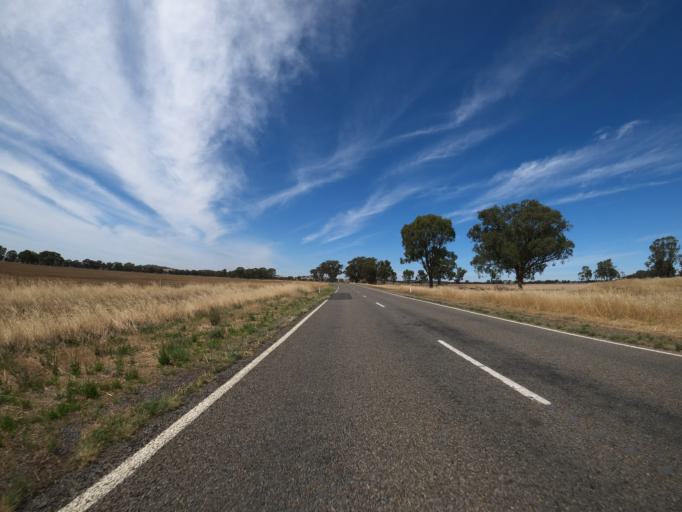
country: AU
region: Victoria
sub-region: Benalla
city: Benalla
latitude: -36.2969
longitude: 145.9523
